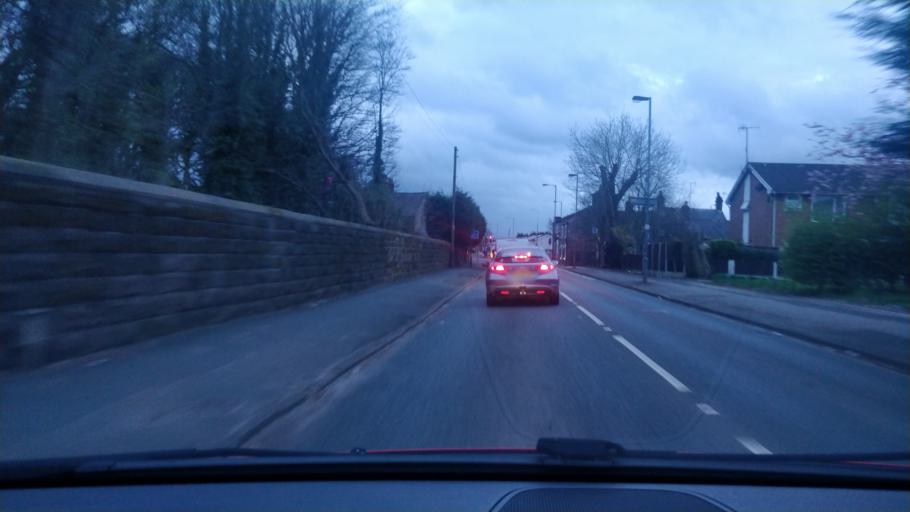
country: GB
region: England
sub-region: Knowsley
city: Knowsley
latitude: 53.4371
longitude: -2.8867
